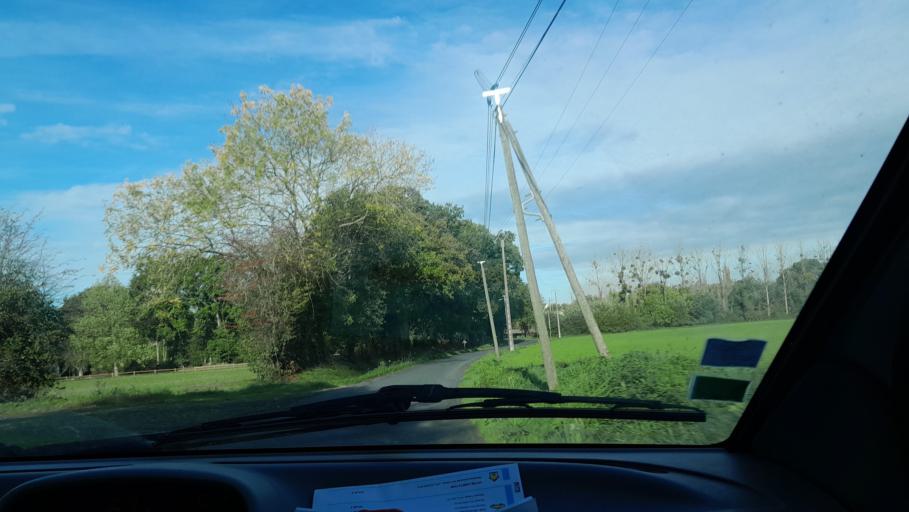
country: FR
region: Lower Normandy
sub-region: Departement de la Manche
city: Pontorson
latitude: 48.5592
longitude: -1.4612
